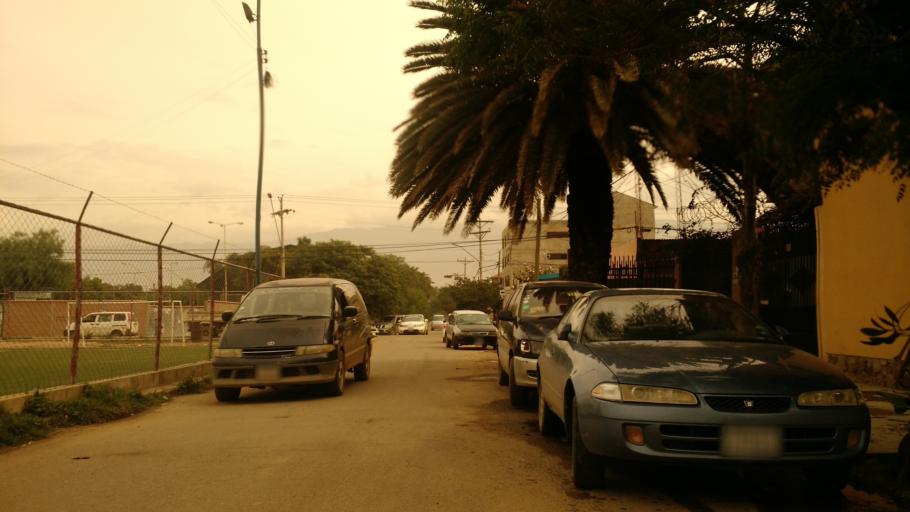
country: BO
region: Cochabamba
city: Cochabamba
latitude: -17.4261
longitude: -66.1558
